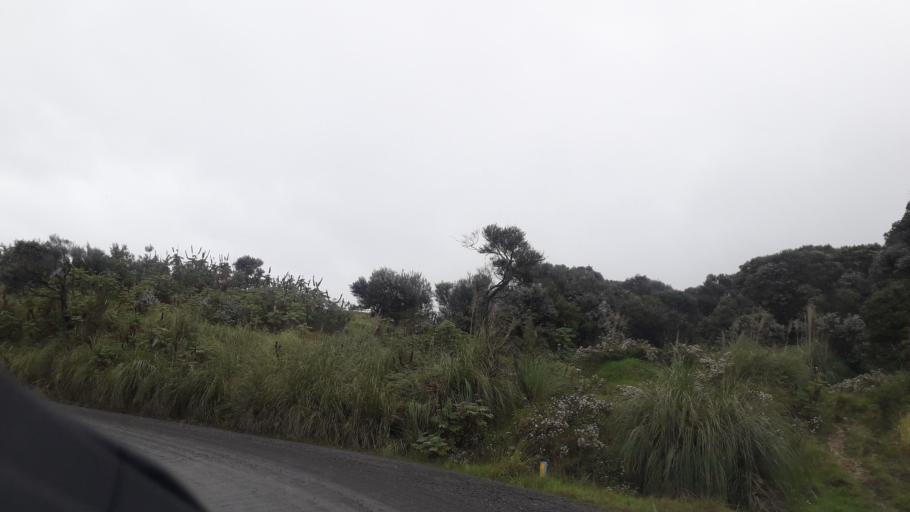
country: NZ
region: Northland
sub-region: Far North District
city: Kaitaia
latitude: -35.4076
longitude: 173.3631
